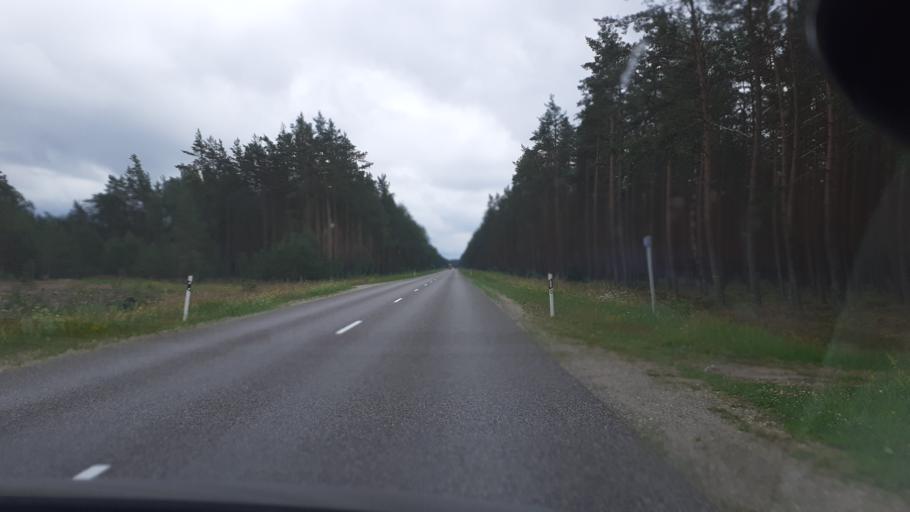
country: LV
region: Ventspils Rajons
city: Piltene
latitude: 57.1320
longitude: 21.7289
